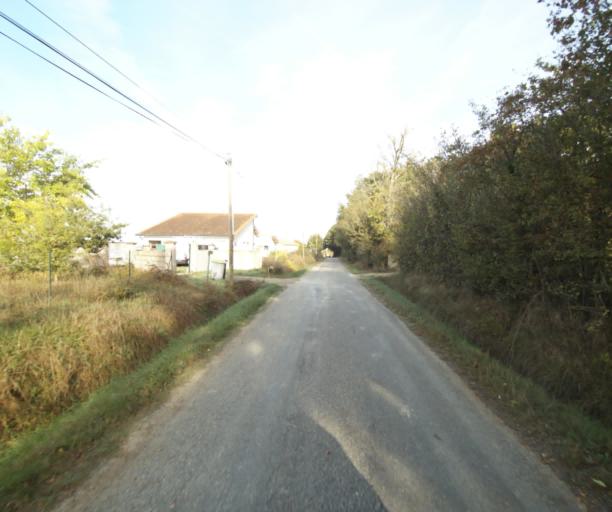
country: FR
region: Midi-Pyrenees
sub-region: Departement de la Haute-Garonne
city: Villemur-sur-Tarn
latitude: 43.9100
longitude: 1.5137
